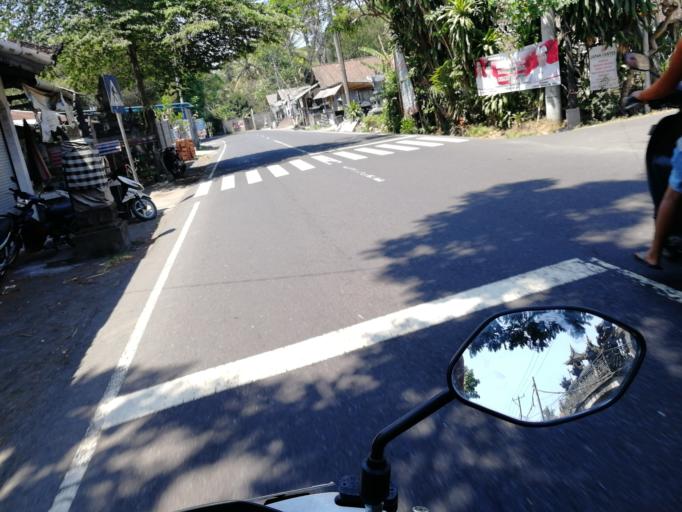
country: ID
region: Bali
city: Abang
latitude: -8.3955
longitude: 115.5969
